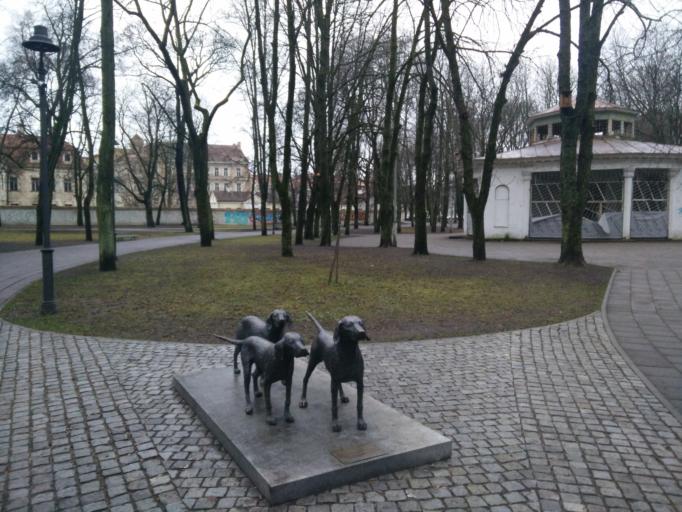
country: LT
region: Vilnius County
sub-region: Vilnius
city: Vilnius
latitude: 54.6861
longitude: 25.2937
